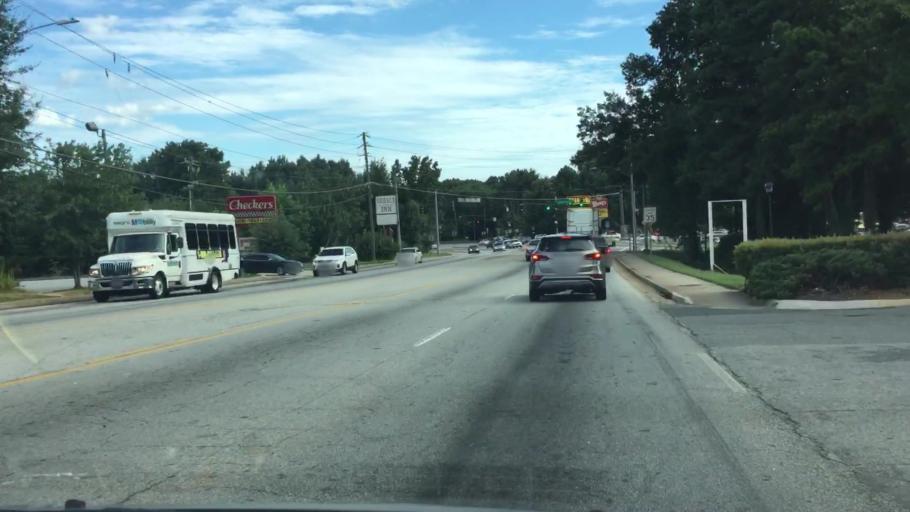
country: US
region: Georgia
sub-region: DeKalb County
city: Gresham Park
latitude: 33.6868
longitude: -84.3108
